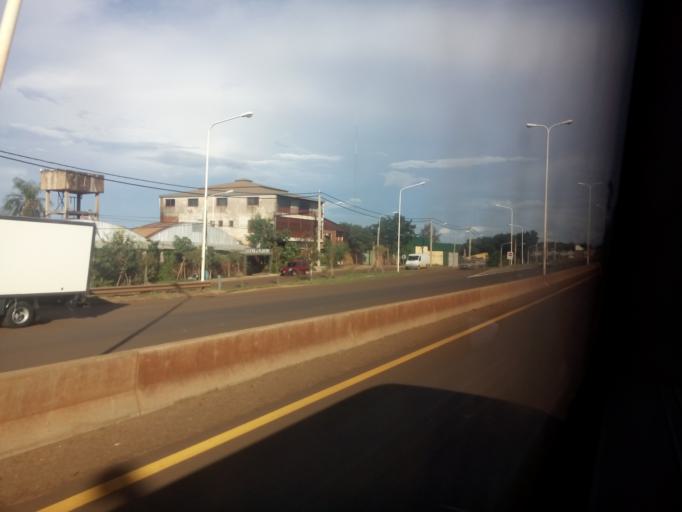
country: AR
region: Misiones
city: Garupa
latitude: -27.4575
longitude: -55.8541
